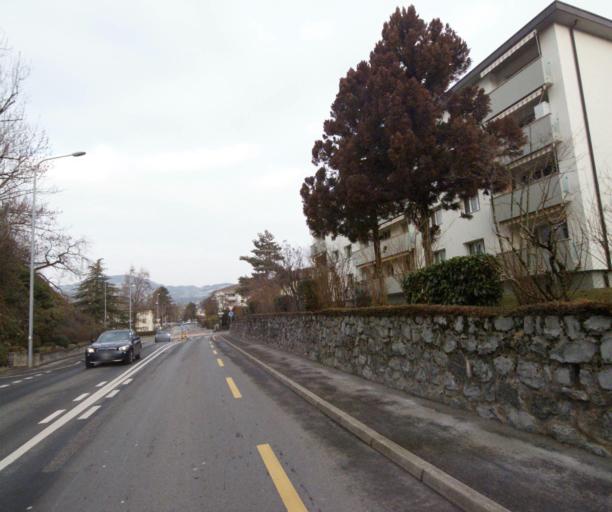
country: CH
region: Vaud
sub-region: Riviera-Pays-d'Enhaut District
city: La Tour-de-Peilz
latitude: 46.4533
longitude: 6.8685
